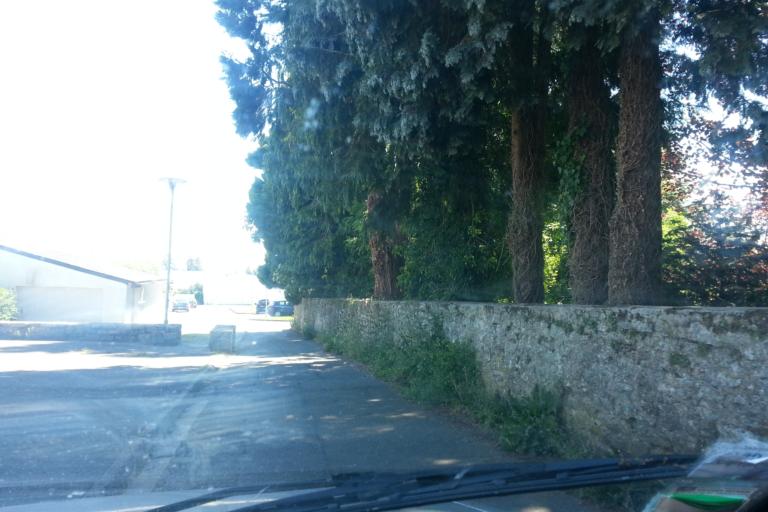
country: FR
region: Brittany
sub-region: Departement du Morbihan
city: Le Faouet
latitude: 48.0316
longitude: -3.4885
